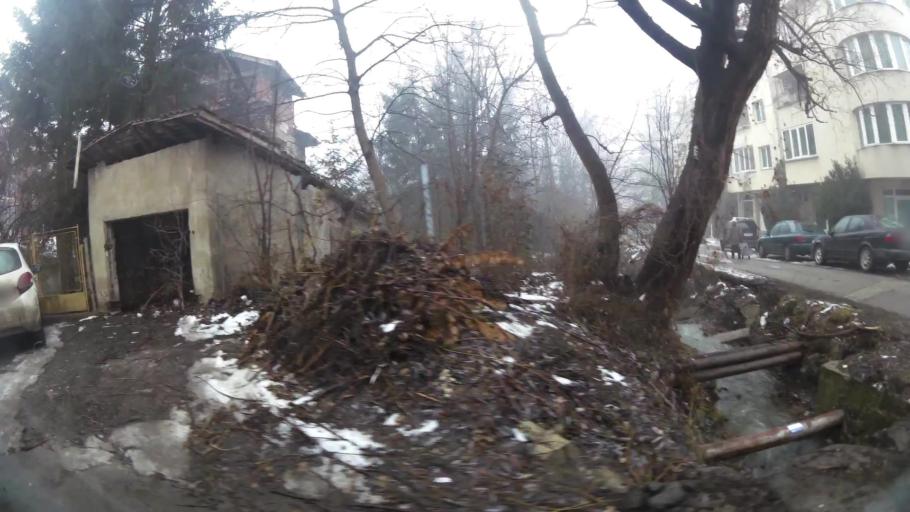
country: BG
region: Sofia-Capital
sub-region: Stolichna Obshtina
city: Sofia
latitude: 42.6615
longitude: 23.2534
